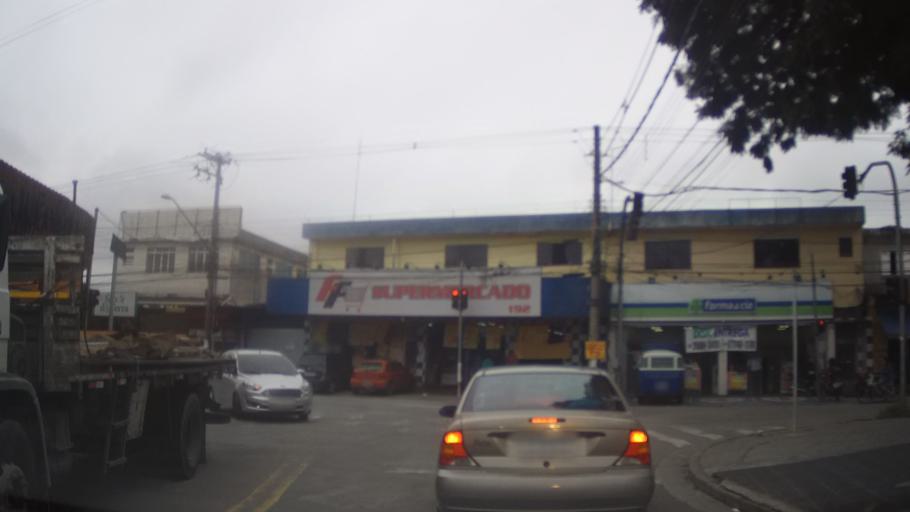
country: BR
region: Sao Paulo
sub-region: Guarulhos
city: Guarulhos
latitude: -23.4386
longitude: -46.5106
